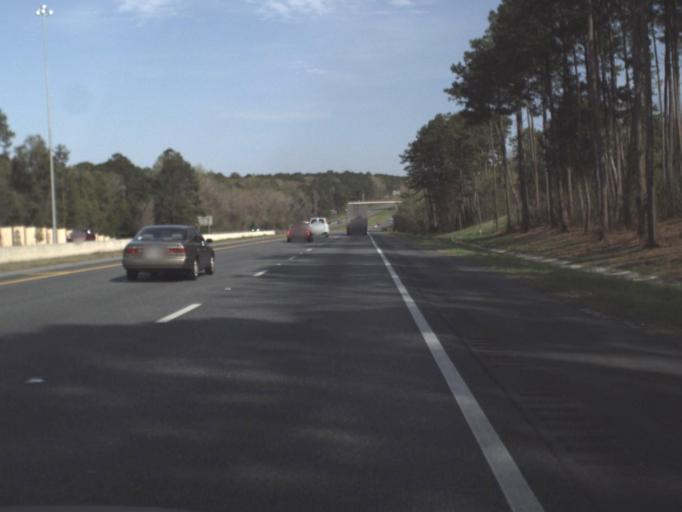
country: US
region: Florida
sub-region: Leon County
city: Tallahassee
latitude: 30.5015
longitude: -84.2379
